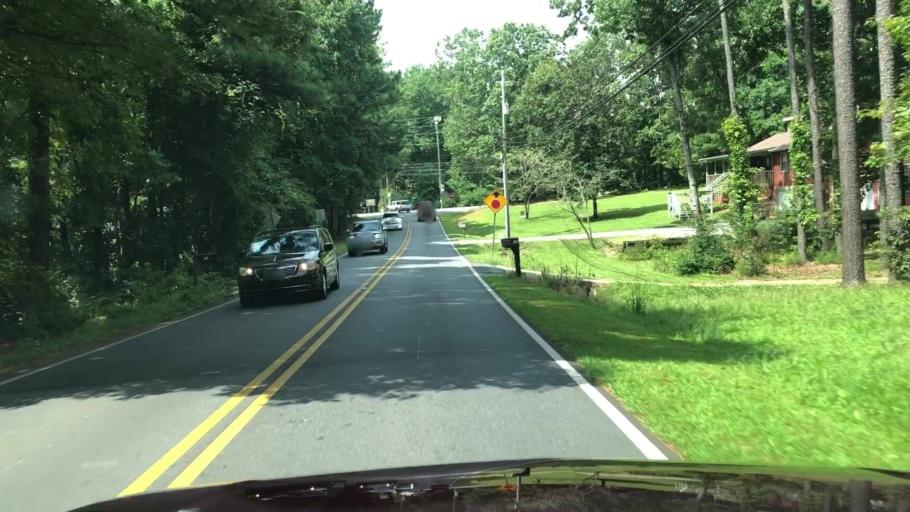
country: US
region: Georgia
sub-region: Cherokee County
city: Woodstock
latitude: 34.1525
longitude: -84.5997
